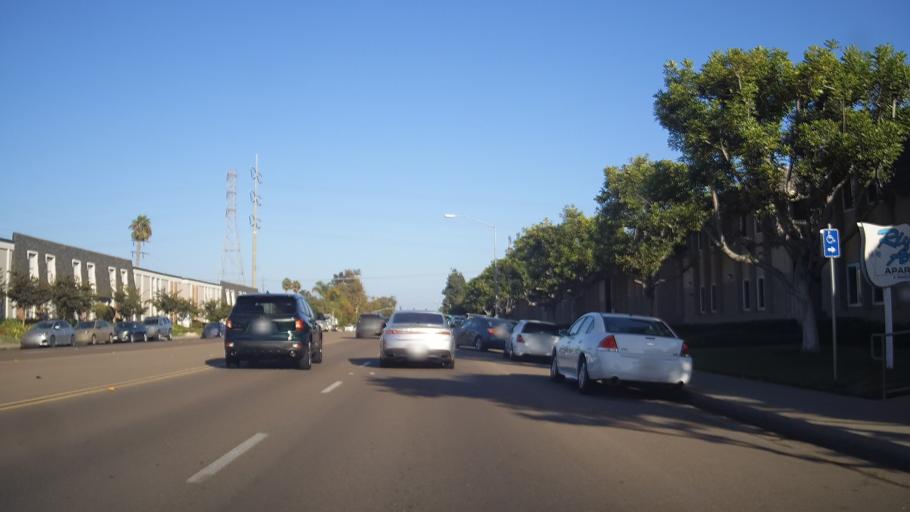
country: US
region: California
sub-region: San Diego County
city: La Jolla
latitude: 32.8344
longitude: -117.1858
